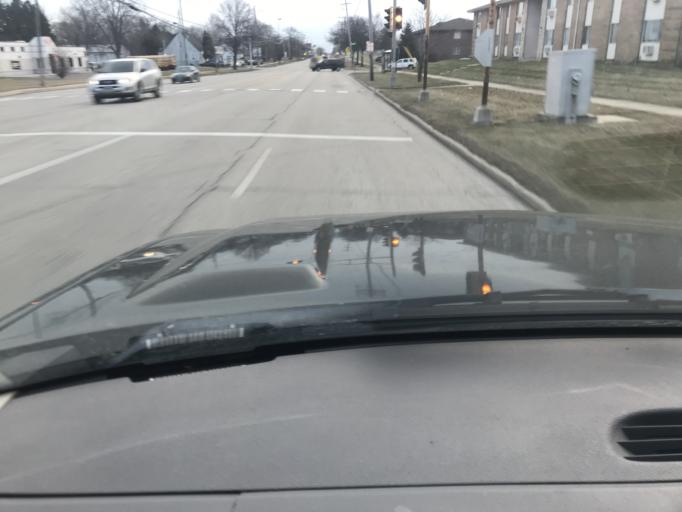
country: US
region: Wisconsin
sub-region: Kenosha County
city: Kenosha
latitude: 42.5885
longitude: -87.8721
